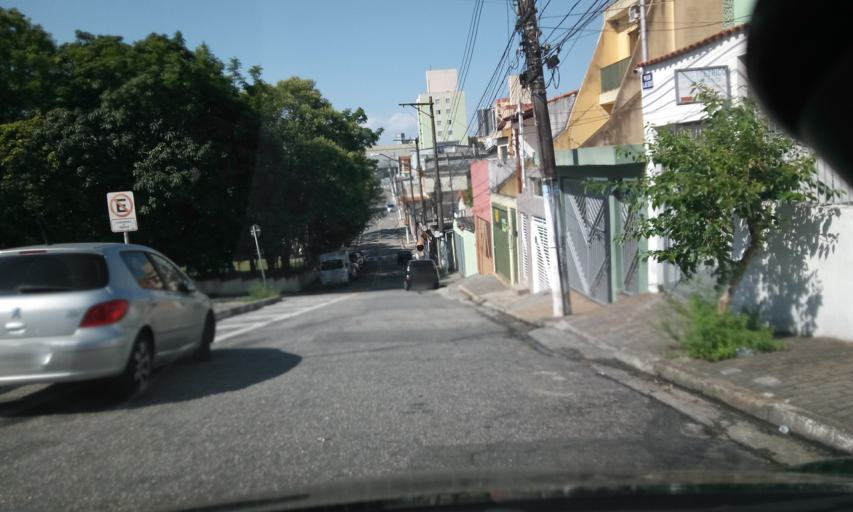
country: BR
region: Sao Paulo
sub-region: Sao Bernardo Do Campo
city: Sao Bernardo do Campo
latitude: -23.6942
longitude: -46.5699
